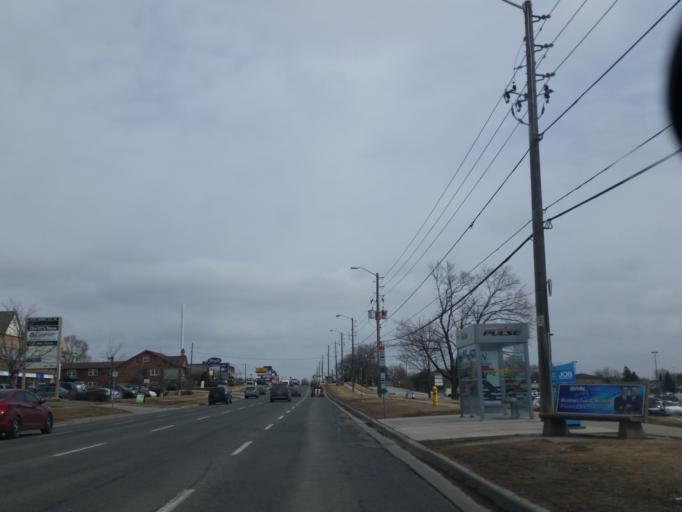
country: CA
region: Ontario
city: Oshawa
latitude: 43.8933
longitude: -78.8823
